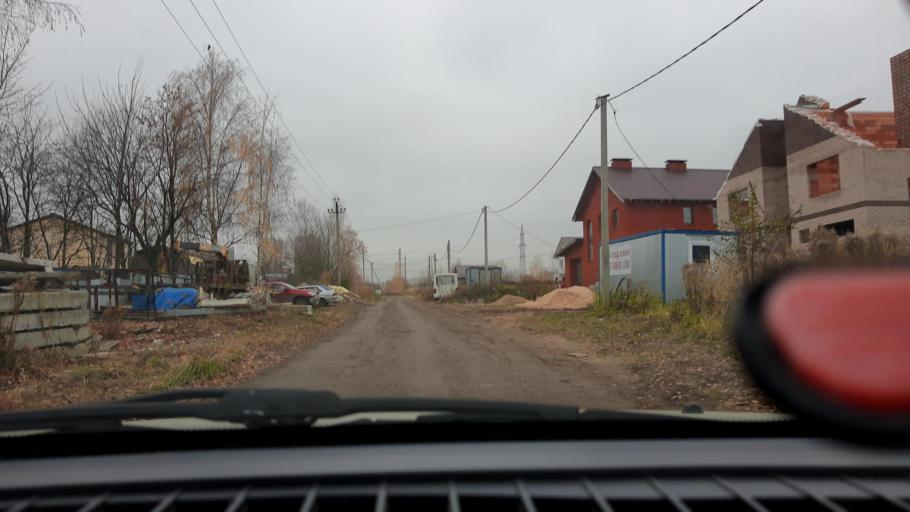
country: RU
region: Nizjnij Novgorod
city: Afonino
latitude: 56.2563
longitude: 44.0553
